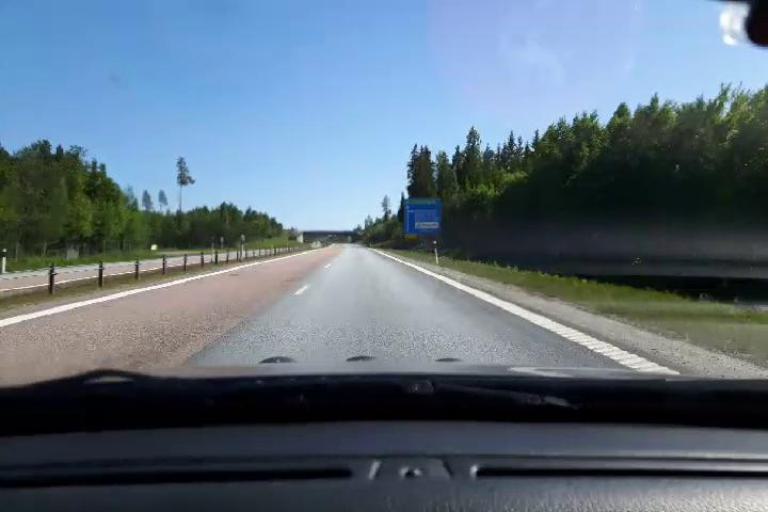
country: SE
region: Gaevleborg
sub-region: Hudiksvalls Kommun
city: Iggesund
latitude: 61.5241
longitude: 16.9743
